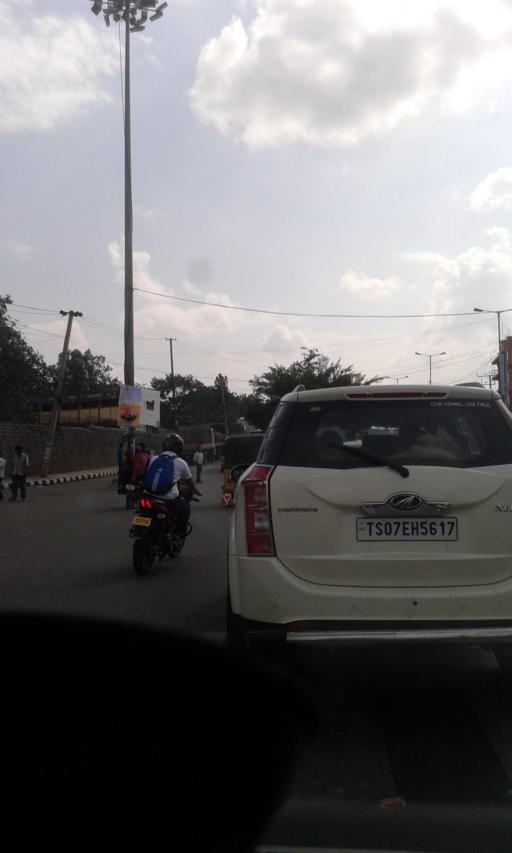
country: IN
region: Telangana
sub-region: Rangareddi
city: Balapur
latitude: 17.3406
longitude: 78.5025
